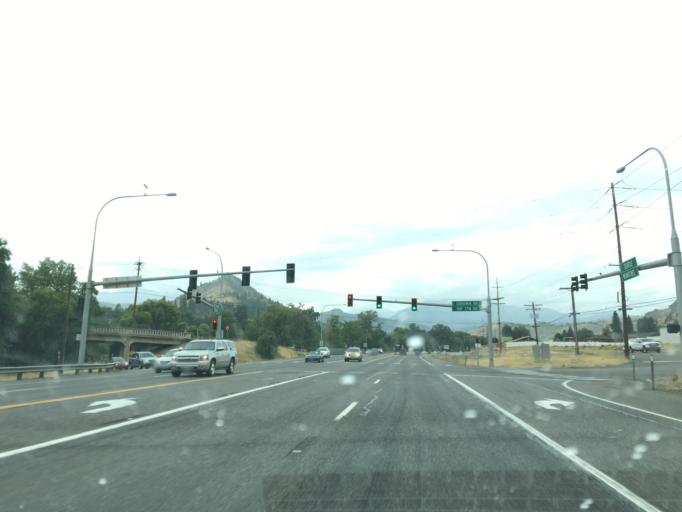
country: US
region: Washington
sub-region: Chelan County
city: Cashmere
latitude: 47.5281
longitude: -120.4881
